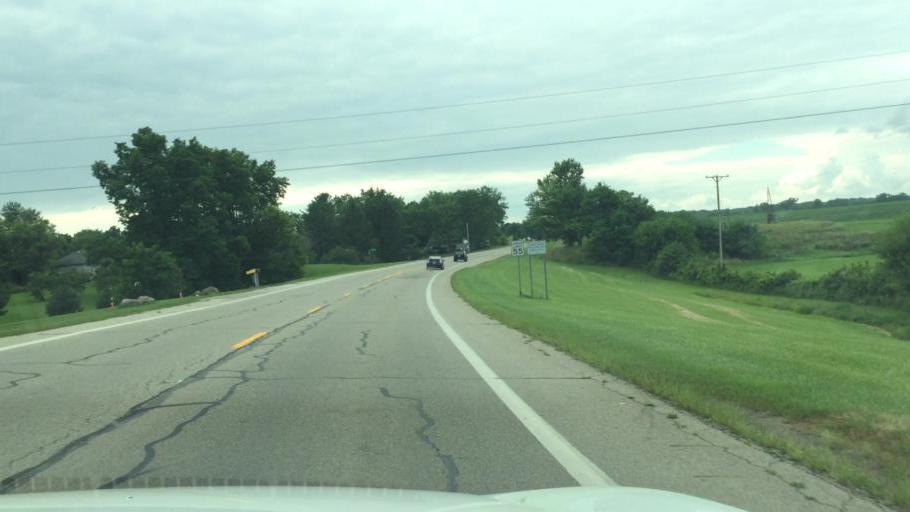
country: US
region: Ohio
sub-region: Champaign County
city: Mechanicsburg
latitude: 40.0759
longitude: -83.5689
